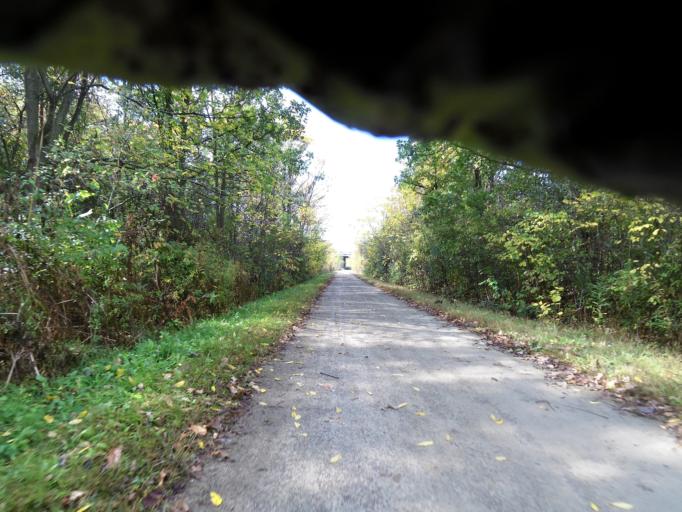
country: CA
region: Ontario
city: Brantford
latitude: 43.1494
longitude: -80.1923
